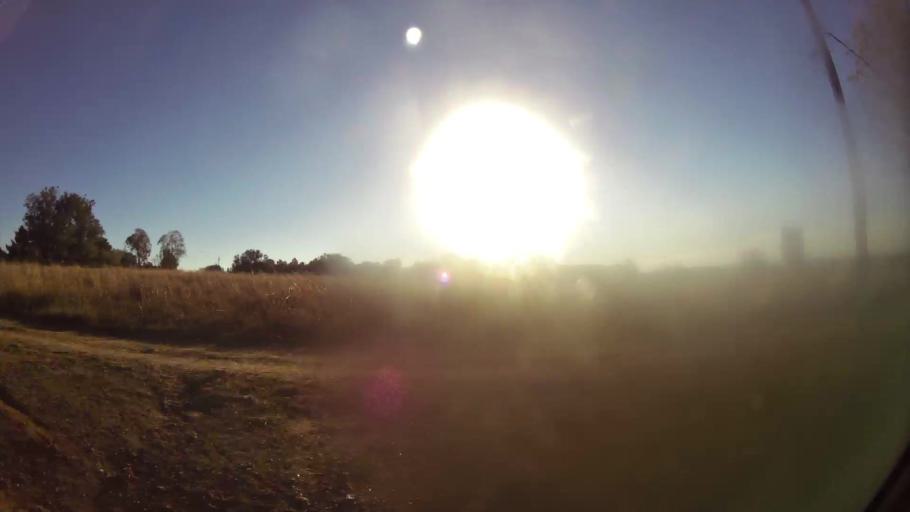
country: ZA
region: Gauteng
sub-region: City of Johannesburg Metropolitan Municipality
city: Midrand
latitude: -26.0127
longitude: 28.1352
